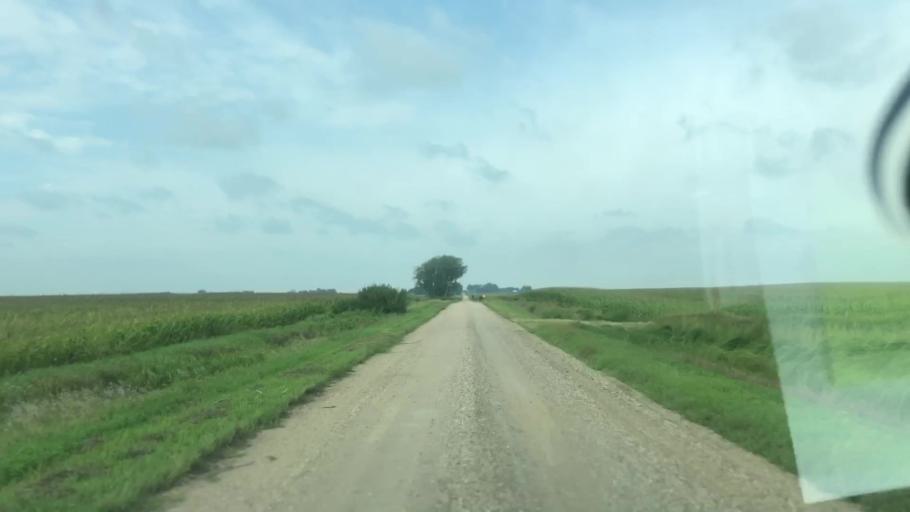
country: US
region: Iowa
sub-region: Lyon County
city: George
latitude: 43.2724
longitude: -95.9306
